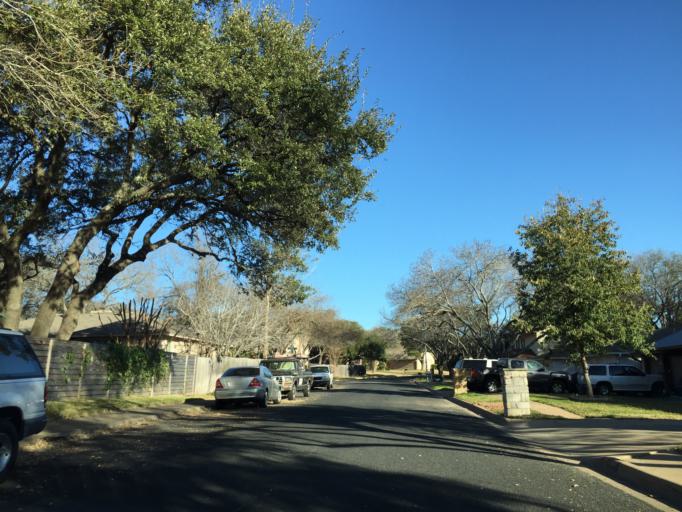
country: US
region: Texas
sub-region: Williamson County
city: Jollyville
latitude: 30.4084
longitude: -97.7400
